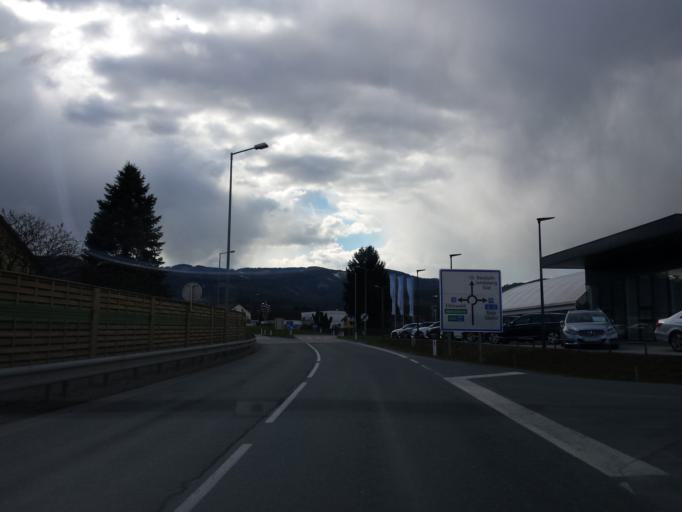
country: AT
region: Styria
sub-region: Politischer Bezirk Deutschlandsberg
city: Deutschlandsberg
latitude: 46.8162
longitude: 15.2371
